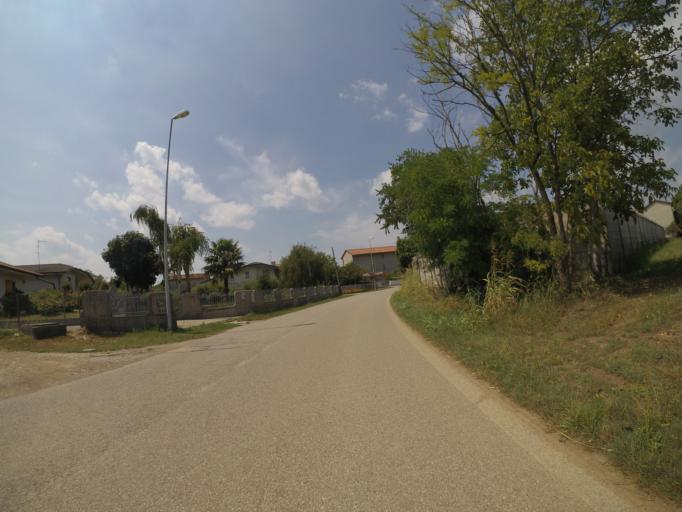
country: IT
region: Friuli Venezia Giulia
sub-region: Provincia di Udine
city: Basiliano
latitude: 45.9805
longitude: 13.0889
